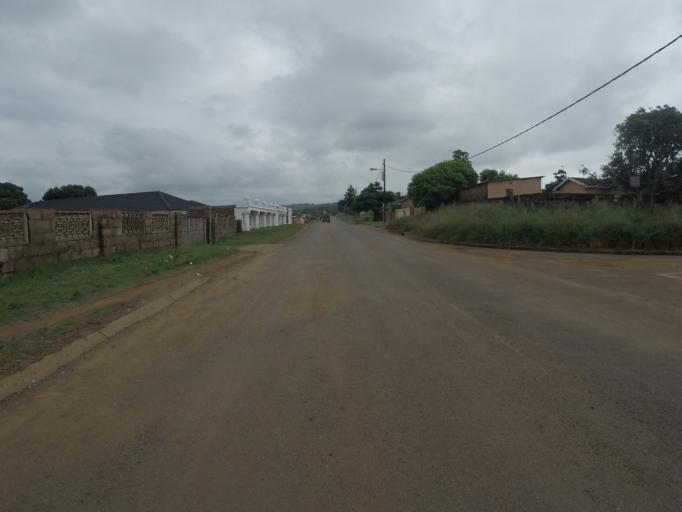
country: ZA
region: KwaZulu-Natal
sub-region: uThungulu District Municipality
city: Empangeni
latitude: -28.7792
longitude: 31.8498
